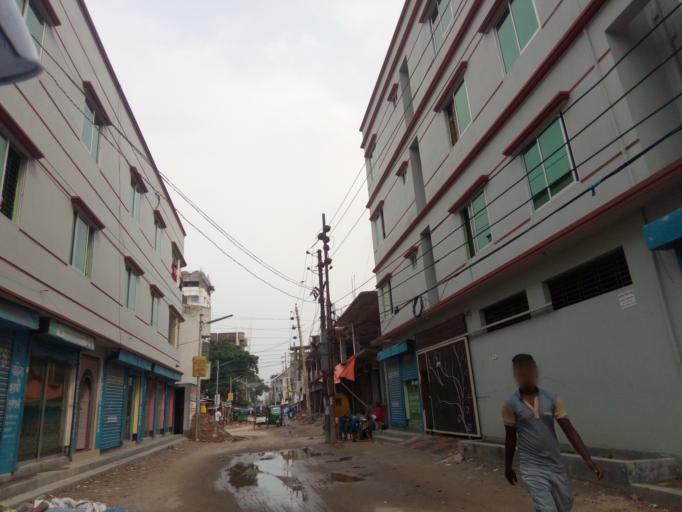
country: BD
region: Dhaka
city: Azimpur
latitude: 23.7500
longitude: 90.3421
